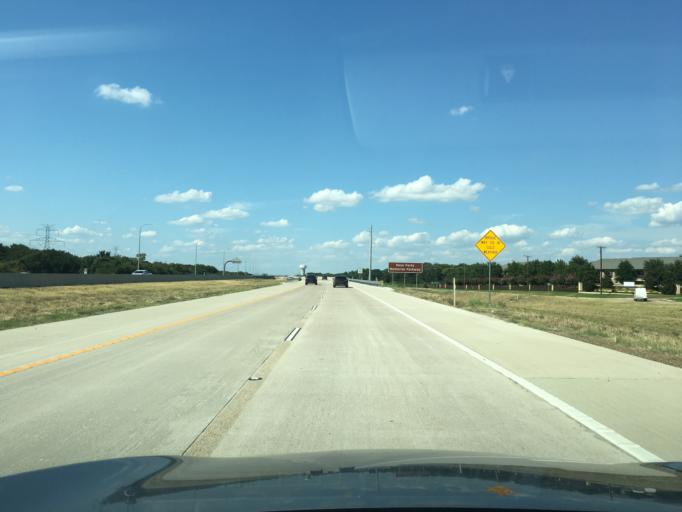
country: US
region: Texas
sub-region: Tarrant County
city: Mansfield
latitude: 32.5842
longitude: -97.0783
